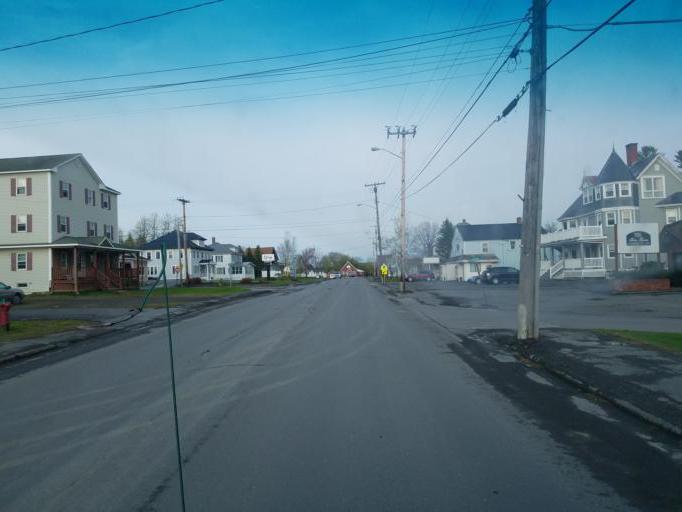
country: US
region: Maine
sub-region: Aroostook County
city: Caribou
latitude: 46.8606
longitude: -68.0079
